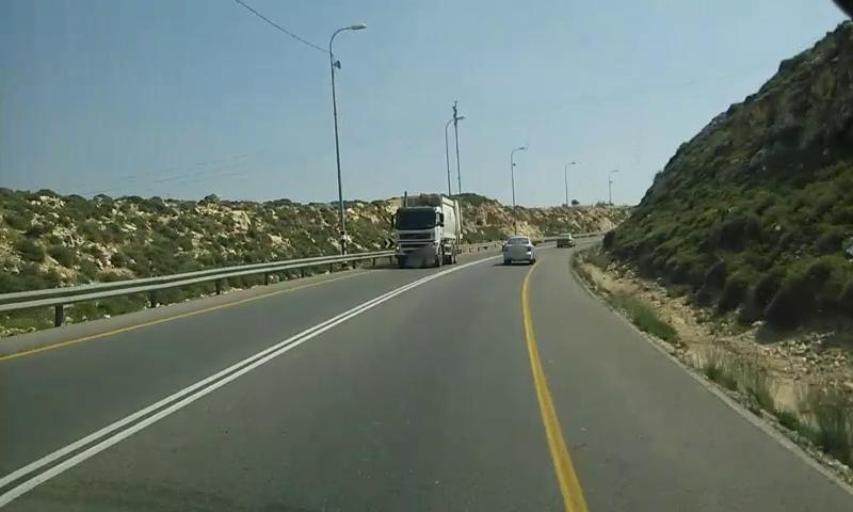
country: PS
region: West Bank
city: Jaba`
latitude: 31.8593
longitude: 35.2658
